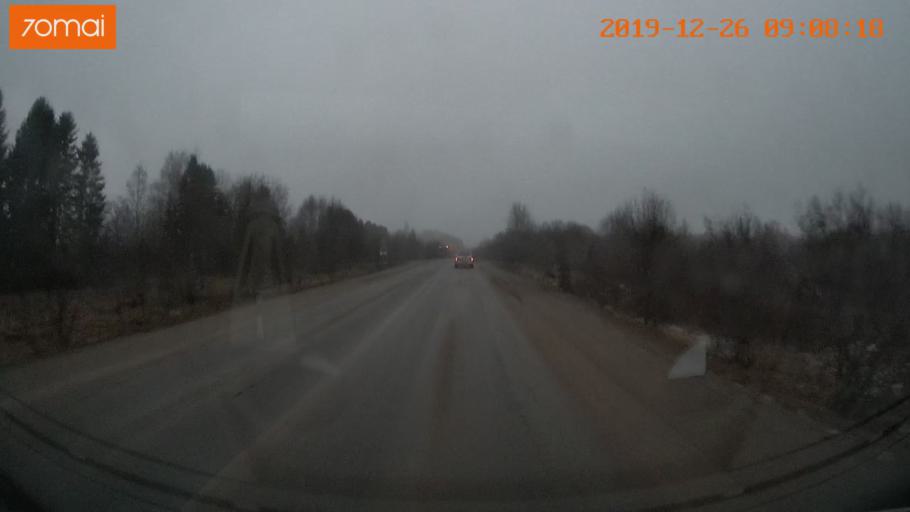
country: RU
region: Vologda
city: Gryazovets
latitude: 58.8552
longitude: 40.2480
